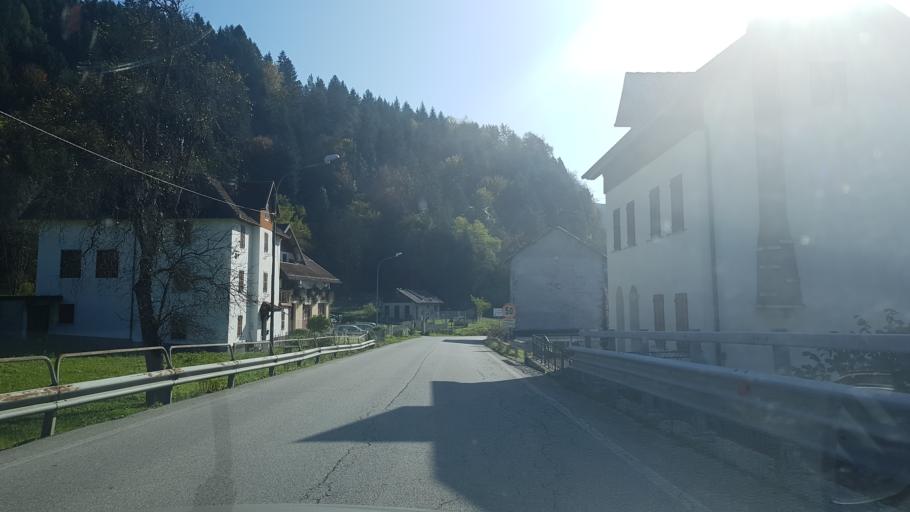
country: IT
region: Friuli Venezia Giulia
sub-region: Provincia di Udine
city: Ovaro
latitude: 46.4776
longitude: 12.8695
